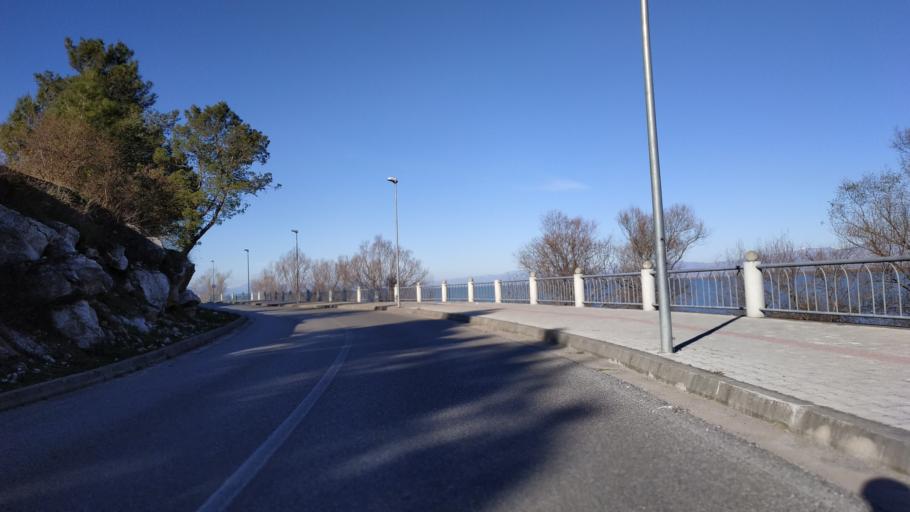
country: AL
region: Shkoder
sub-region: Rrethi i Shkodres
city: Berdica e Madhe
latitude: 42.0567
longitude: 19.4669
